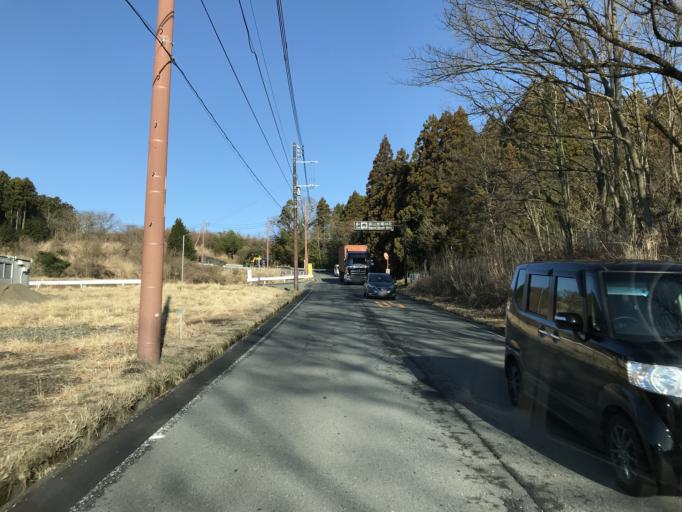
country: JP
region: Shizuoka
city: Gotemba
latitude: 35.2633
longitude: 138.8534
